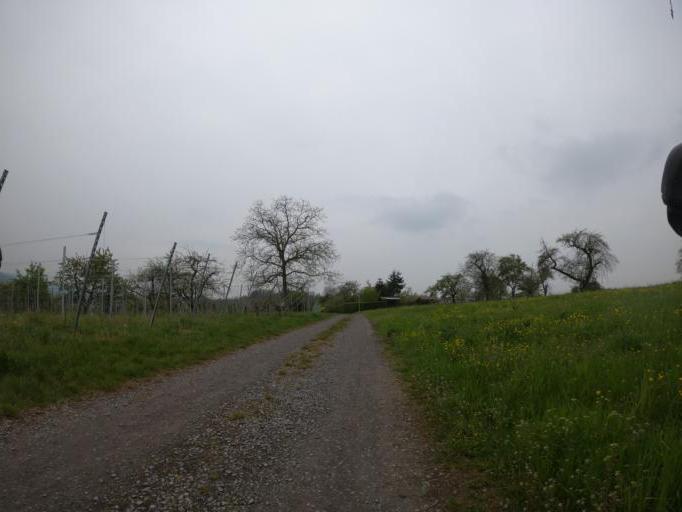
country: DE
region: Baden-Wuerttemberg
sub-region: Regierungsbezirk Stuttgart
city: Oberriexingen
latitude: 48.9449
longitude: 9.0614
